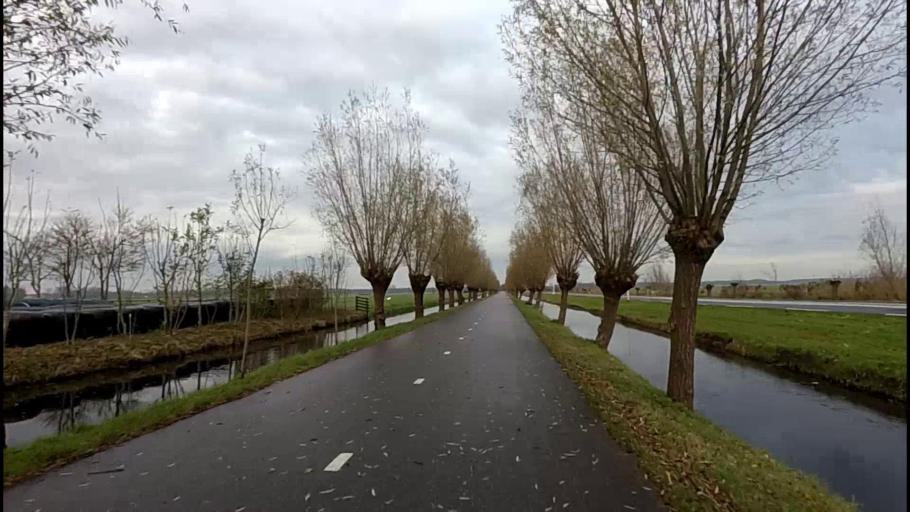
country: NL
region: South Holland
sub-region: Molenwaard
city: Nieuw-Lekkerland
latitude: 51.9103
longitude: 4.6848
